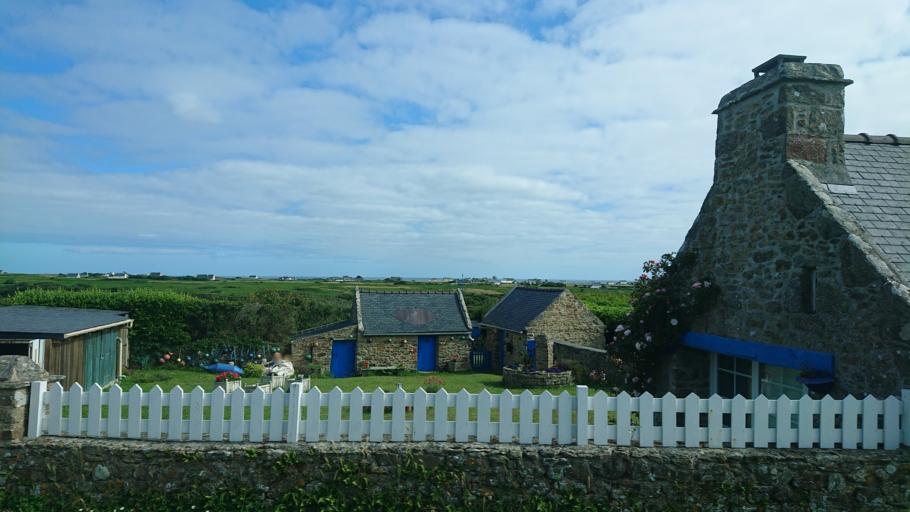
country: FR
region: Brittany
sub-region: Departement du Finistere
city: Porspoder
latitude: 48.4645
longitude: -5.0798
